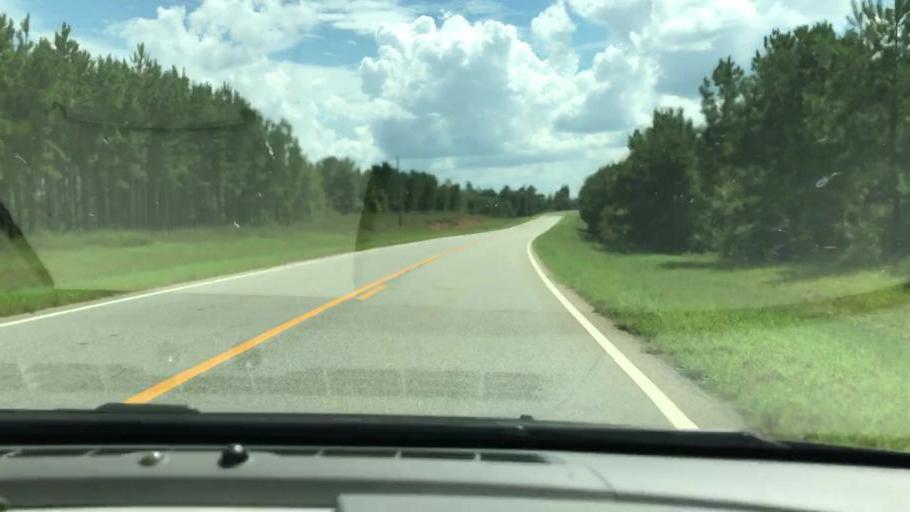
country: US
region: Georgia
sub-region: Quitman County
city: Georgetown
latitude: 31.9153
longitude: -85.0590
